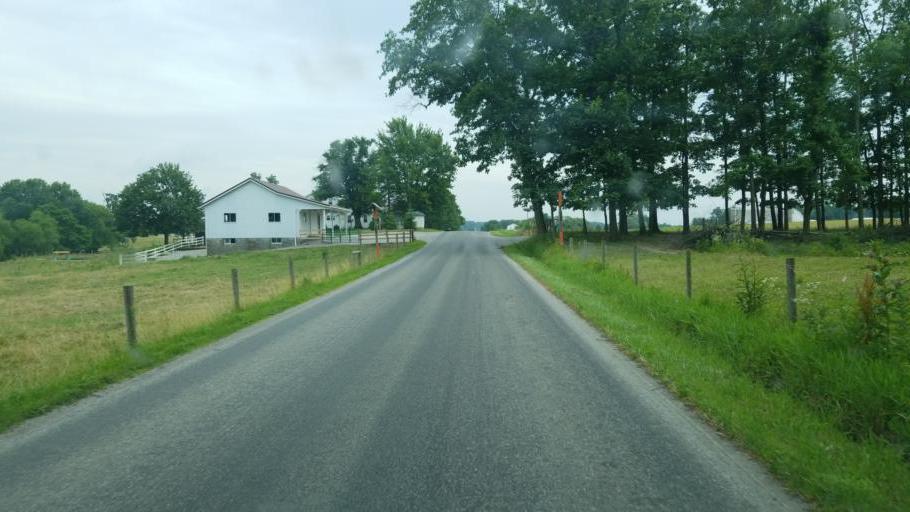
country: US
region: Ohio
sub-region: Wayne County
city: Apple Creek
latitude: 40.7715
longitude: -81.7752
